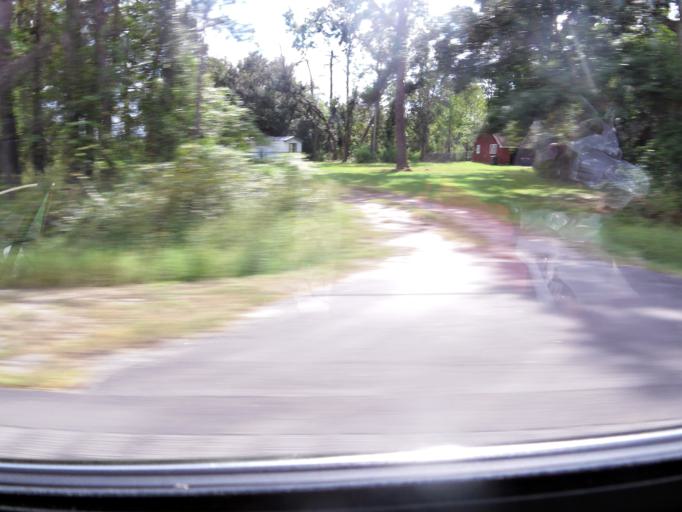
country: US
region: Georgia
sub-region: Glynn County
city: Dock Junction
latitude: 31.1769
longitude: -81.6256
